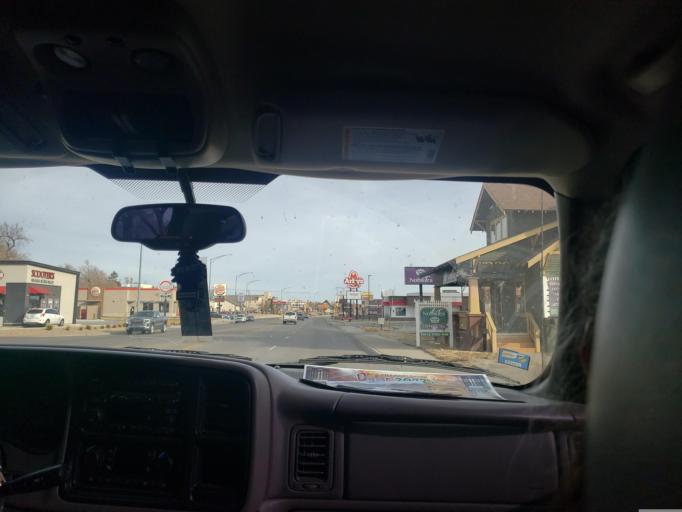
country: US
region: Kansas
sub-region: Ford County
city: Dodge City
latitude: 37.7533
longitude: -100.0266
